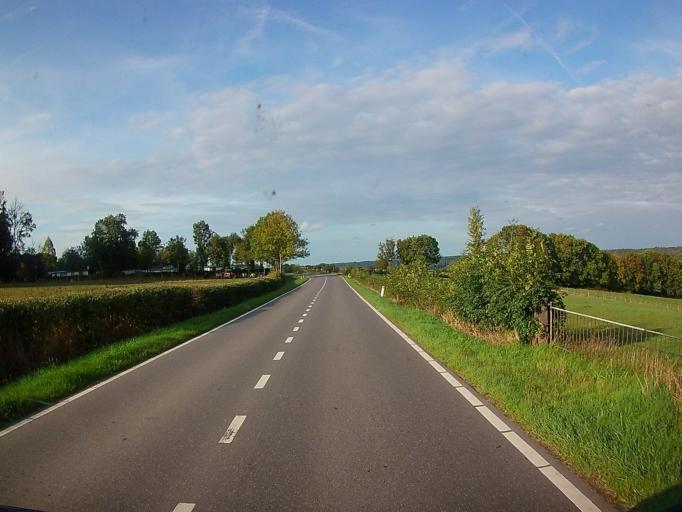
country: BE
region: Wallonia
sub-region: Province de Liege
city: Aubel
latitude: 50.7275
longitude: 5.8678
